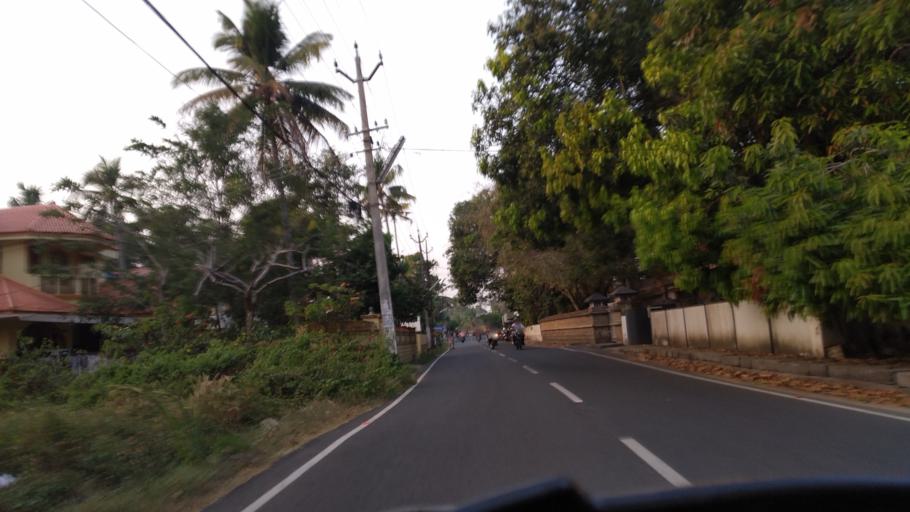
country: IN
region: Kerala
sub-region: Ernakulam
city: Elur
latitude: 10.1345
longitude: 76.2318
